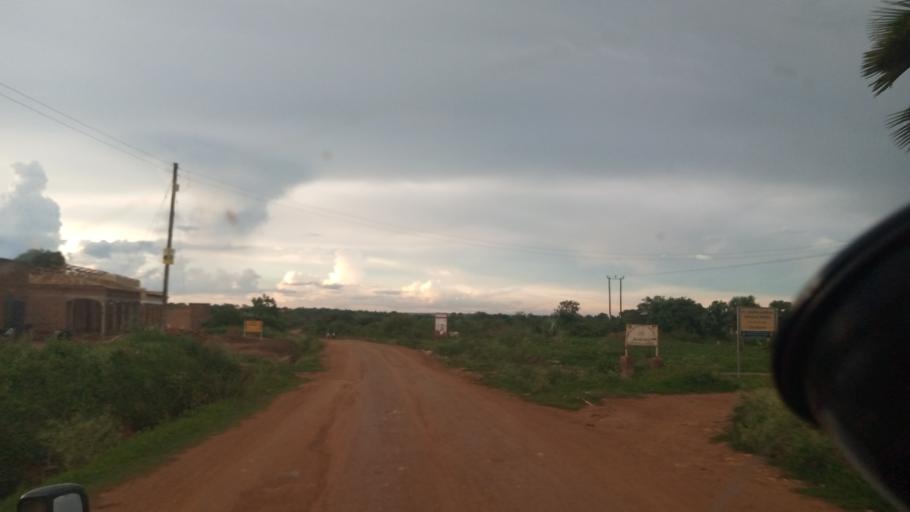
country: UG
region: Northern Region
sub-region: Kole District
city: Kole
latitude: 2.4908
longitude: 32.9347
